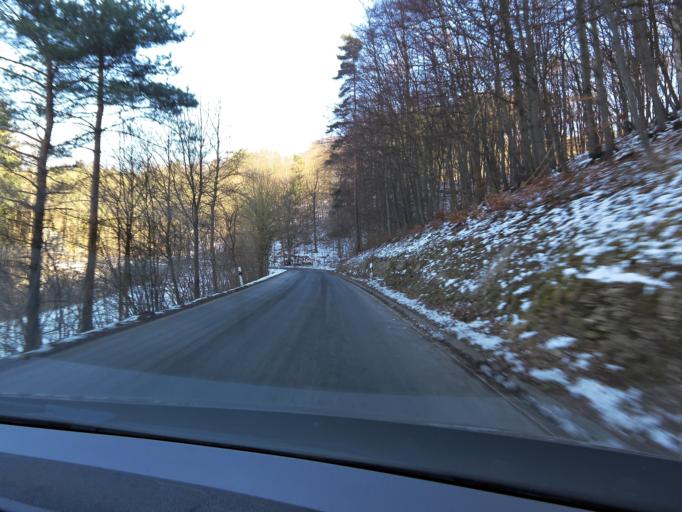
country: DE
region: Hesse
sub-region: Regierungsbezirk Kassel
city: Sontra
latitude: 51.0772
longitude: 10.0096
